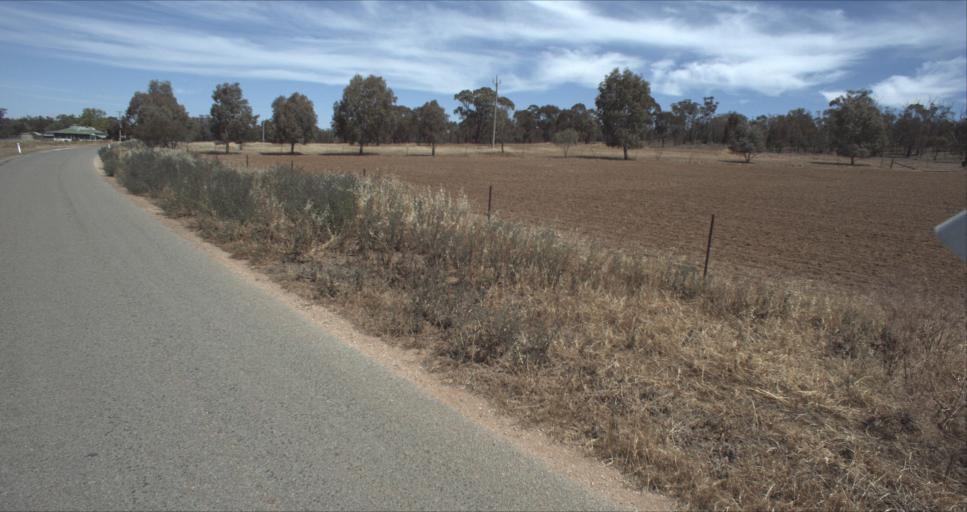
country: AU
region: New South Wales
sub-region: Leeton
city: Leeton
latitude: -34.5998
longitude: 146.4792
